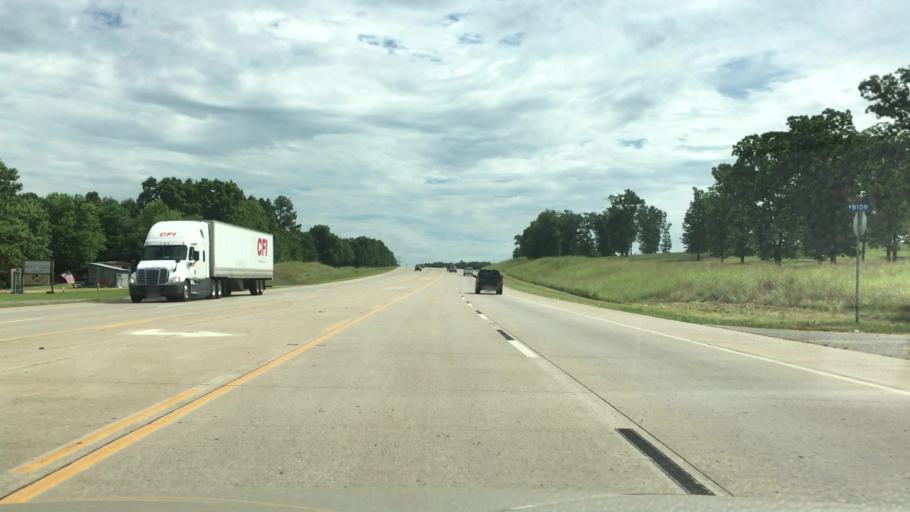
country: US
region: Oklahoma
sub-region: Cherokee County
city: Park Hill
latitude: 35.8419
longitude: -95.0322
